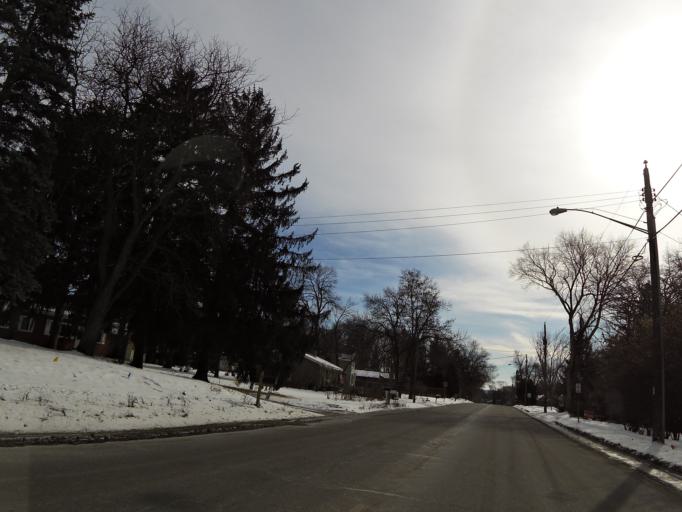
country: US
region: Wisconsin
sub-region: Saint Croix County
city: North Hudson
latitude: 45.0000
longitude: -92.7555
